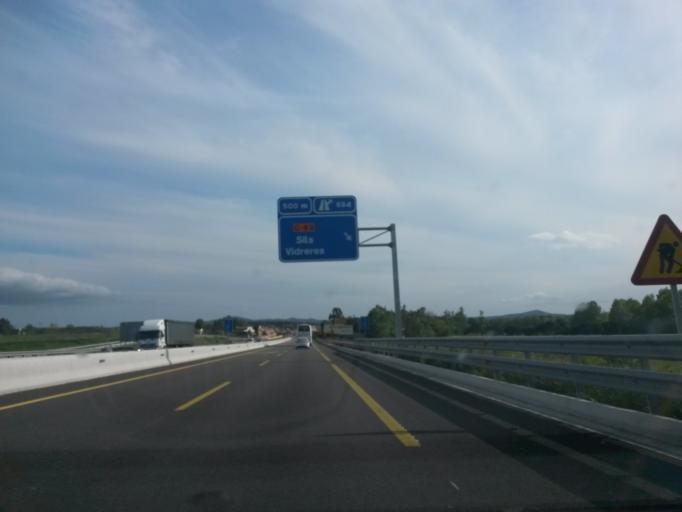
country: ES
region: Catalonia
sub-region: Provincia de Girona
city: Sils
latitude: 41.8130
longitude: 2.7639
